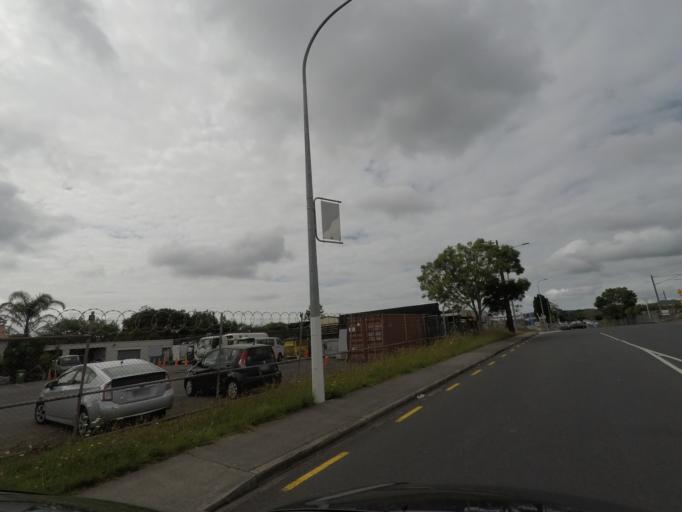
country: NZ
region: Auckland
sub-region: Auckland
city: Waitakere
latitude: -36.8905
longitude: 174.6318
